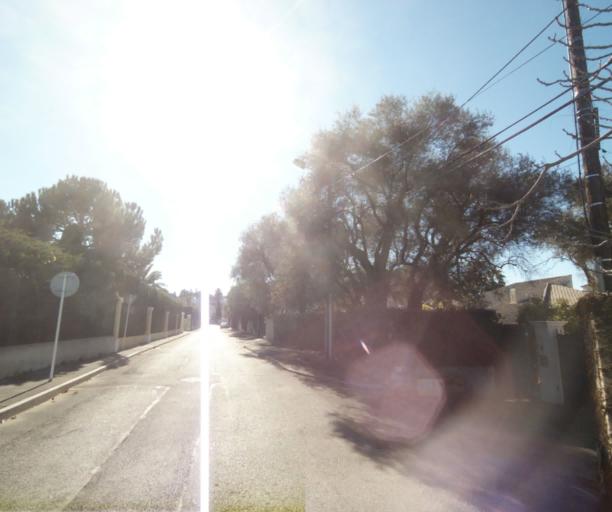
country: FR
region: Provence-Alpes-Cote d'Azur
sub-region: Departement des Alpes-Maritimes
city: Antibes
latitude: 43.5541
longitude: 7.1252
